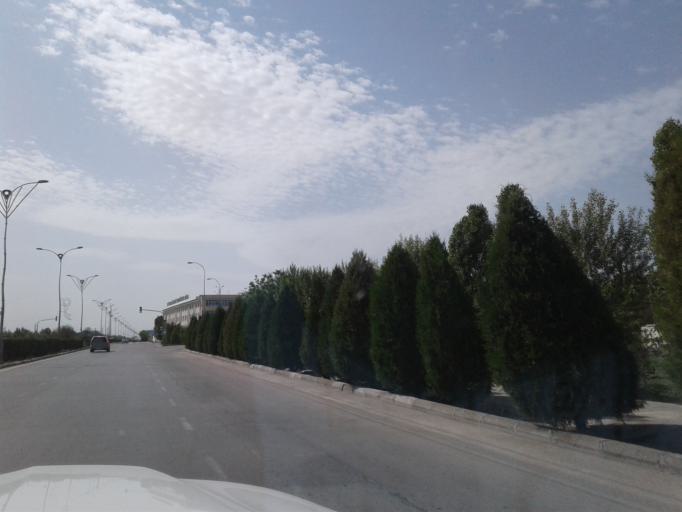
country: TM
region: Dasoguz
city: Dasoguz
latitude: 41.8293
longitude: 59.9469
